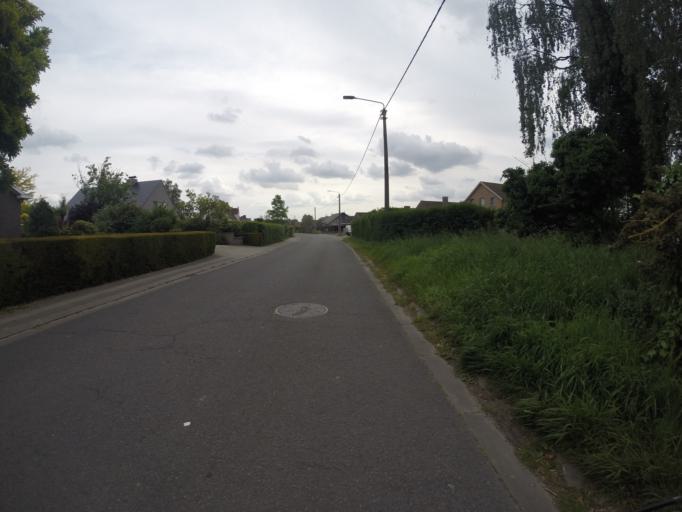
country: BE
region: Flanders
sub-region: Provincie West-Vlaanderen
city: Ruiselede
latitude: 51.0391
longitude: 3.3863
